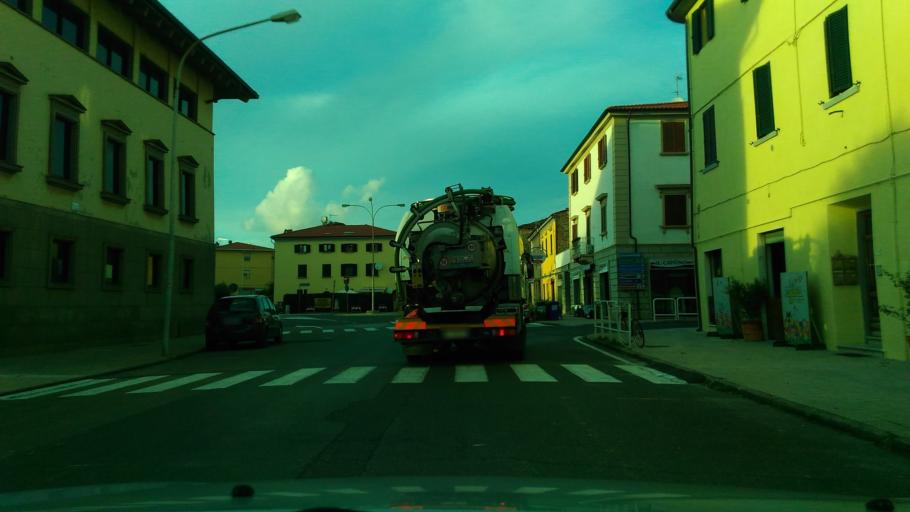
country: IT
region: Tuscany
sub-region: Provincia di Livorno
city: S.P. in Palazzi
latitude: 43.3266
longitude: 10.5077
